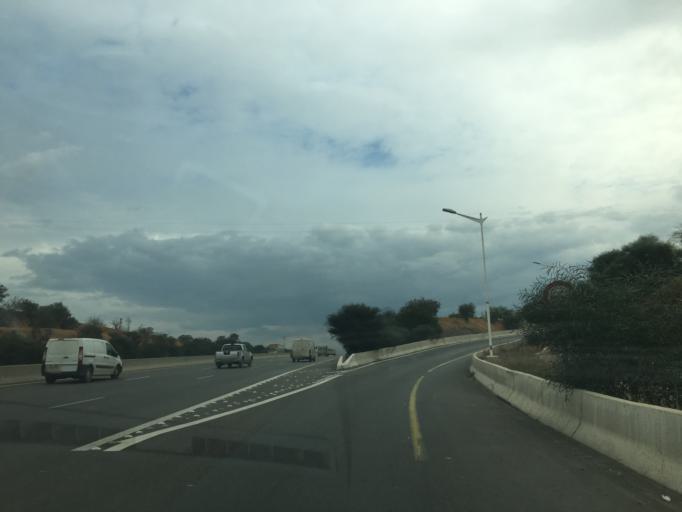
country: DZ
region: Bouira
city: Bouira
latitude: 36.3118
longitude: 4.0590
